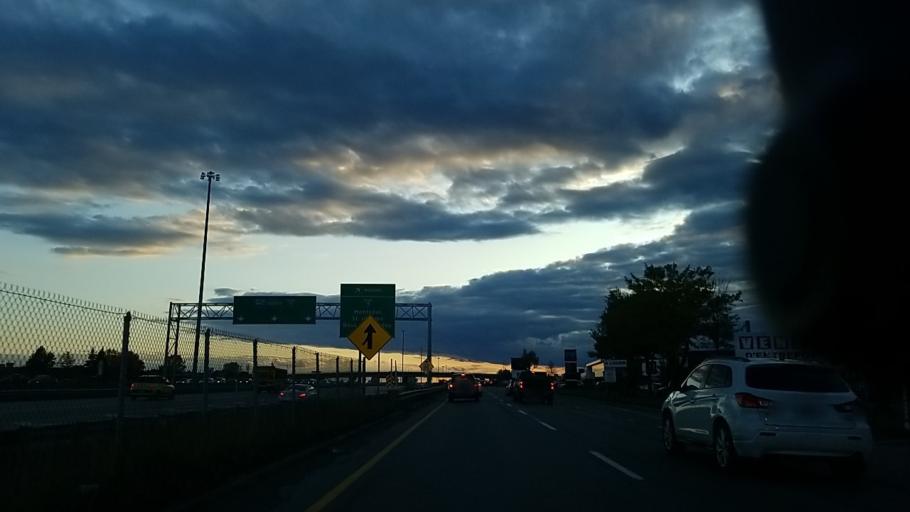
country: CA
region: Quebec
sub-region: Laval
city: Laval
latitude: 45.5822
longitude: -73.7418
